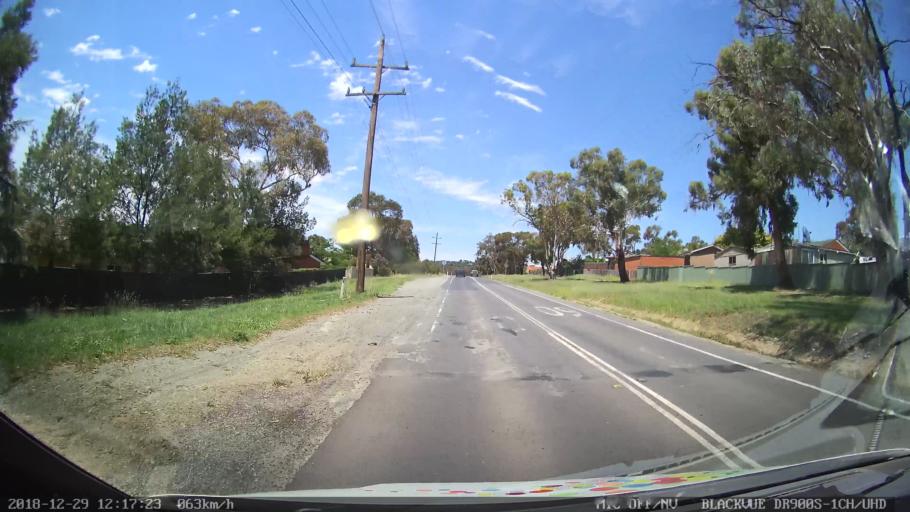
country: AU
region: New South Wales
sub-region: Queanbeyan
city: Queanbeyan
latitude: -35.3747
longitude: 149.2336
